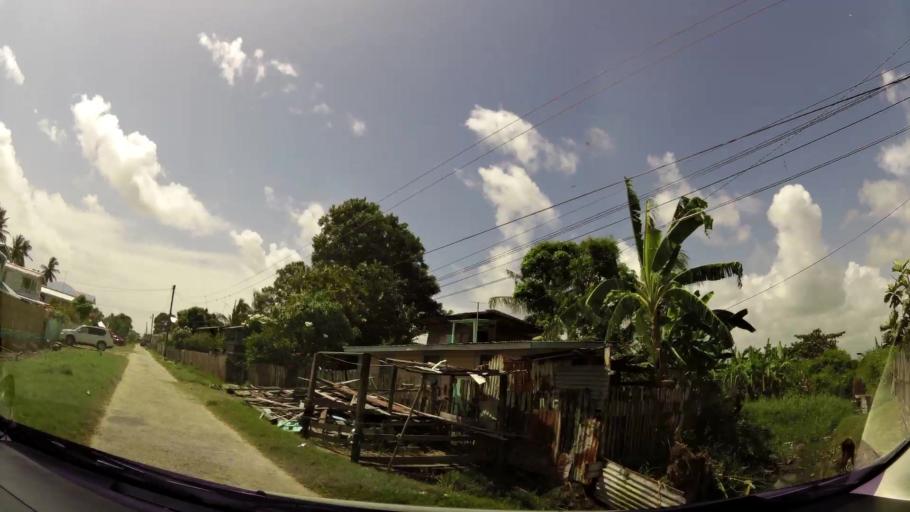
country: GY
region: Demerara-Mahaica
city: Mahaica Village
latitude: 6.7625
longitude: -58.0109
